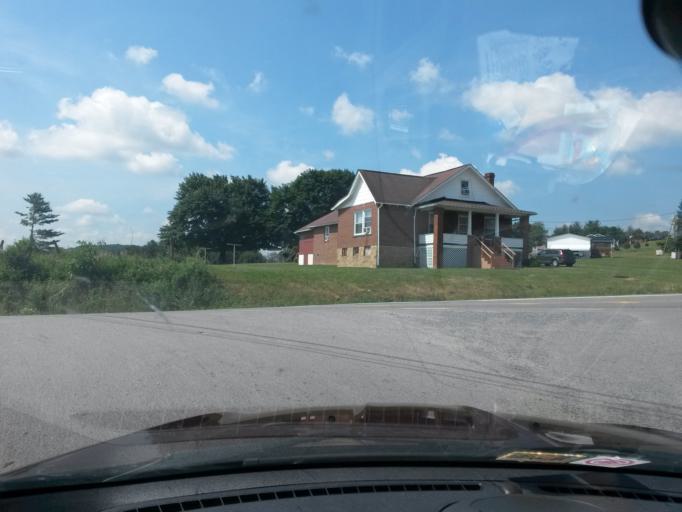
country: US
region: West Virginia
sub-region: Mercer County
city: Princeton
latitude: 37.3924
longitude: -81.1185
